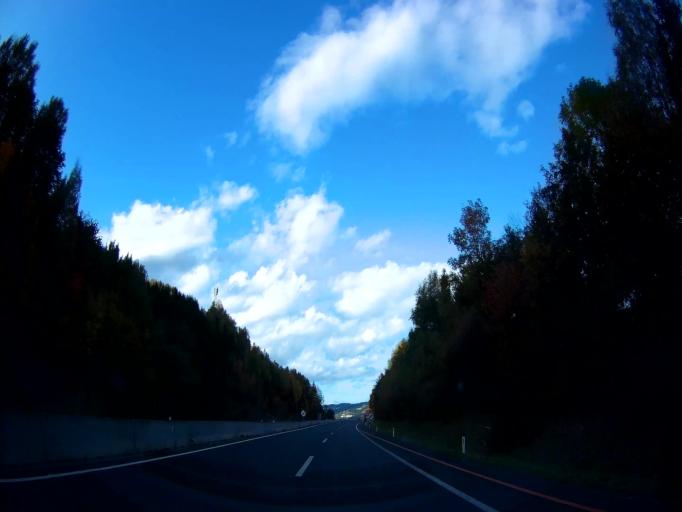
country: AT
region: Carinthia
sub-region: Politischer Bezirk Wolfsberg
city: Wolfsberg
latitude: 46.8574
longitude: 14.8354
